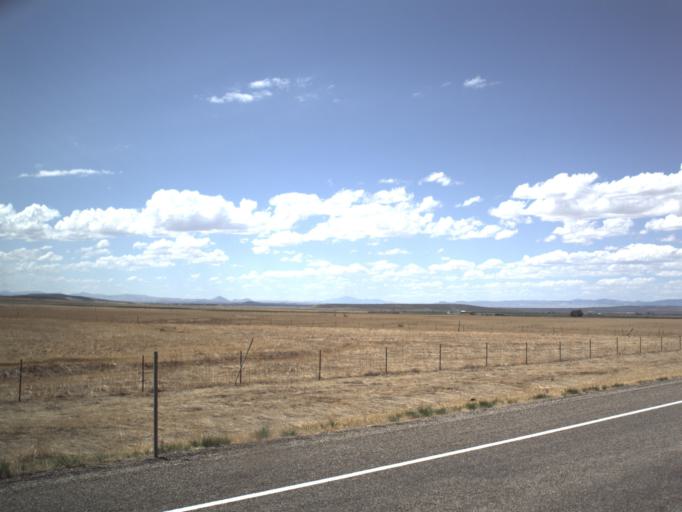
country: US
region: Utah
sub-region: Millard County
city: Fillmore
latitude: 39.1144
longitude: -112.2979
